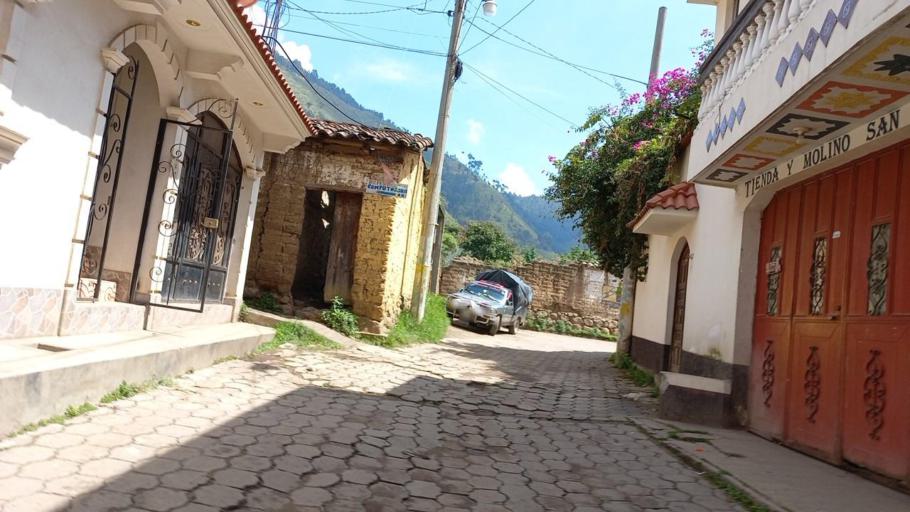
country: GT
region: Totonicapan
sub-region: Municipio de San Andres Xecul
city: San Andres Xecul
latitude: 14.9067
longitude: -91.4821
